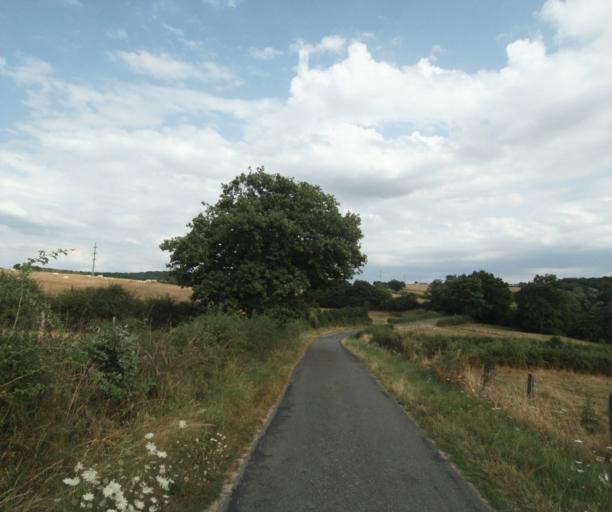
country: FR
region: Bourgogne
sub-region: Departement de Saone-et-Loire
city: Gueugnon
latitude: 46.5993
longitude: 4.0908
